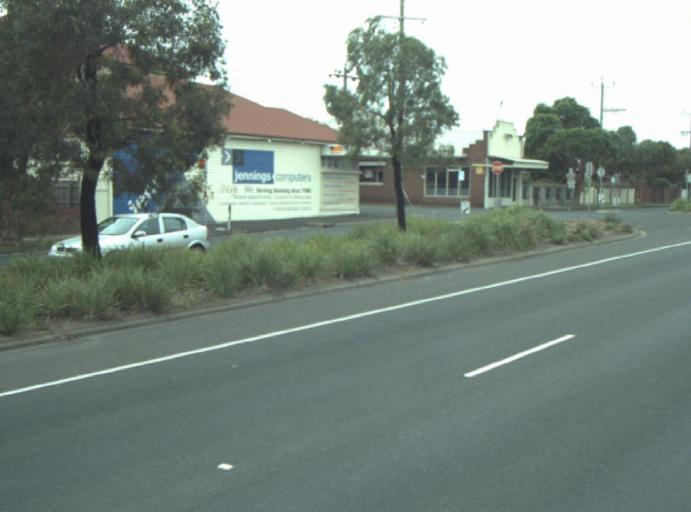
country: AU
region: Victoria
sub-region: Greater Geelong
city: Geelong West
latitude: -38.1299
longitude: 144.3514
